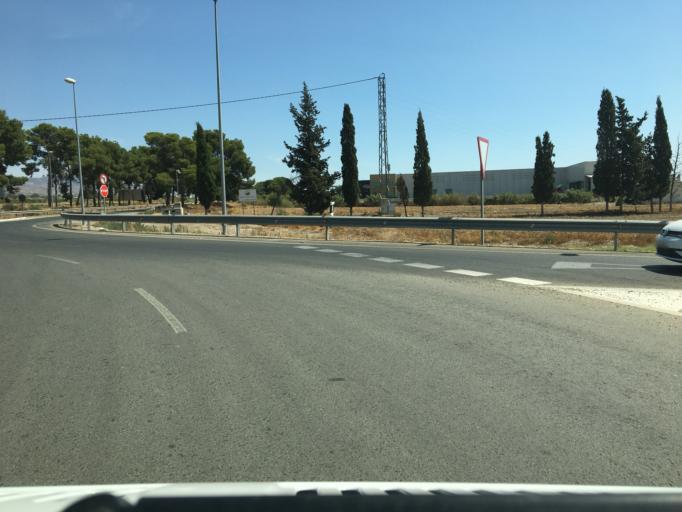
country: ES
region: Andalusia
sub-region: Provincia de Almeria
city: Huercal-Overa
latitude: 37.4160
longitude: -1.9245
